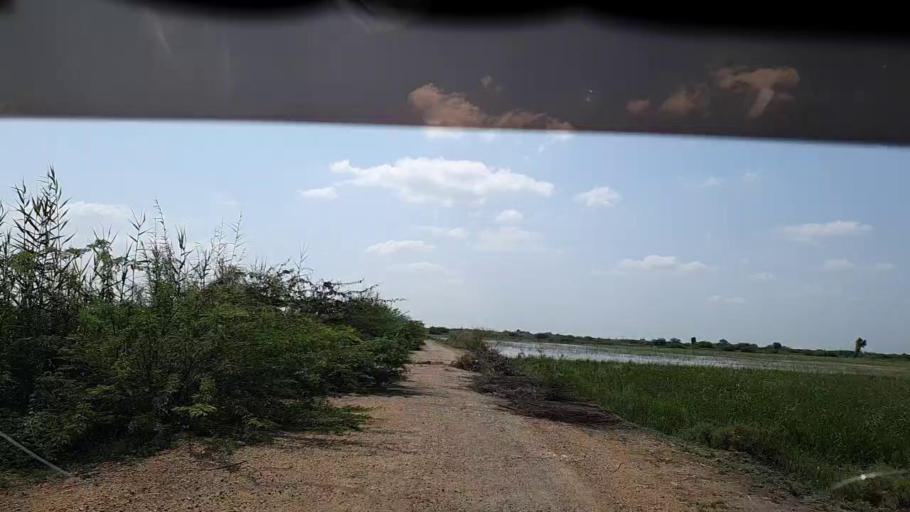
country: PK
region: Sindh
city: Kadhan
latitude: 24.5935
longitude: 69.0275
